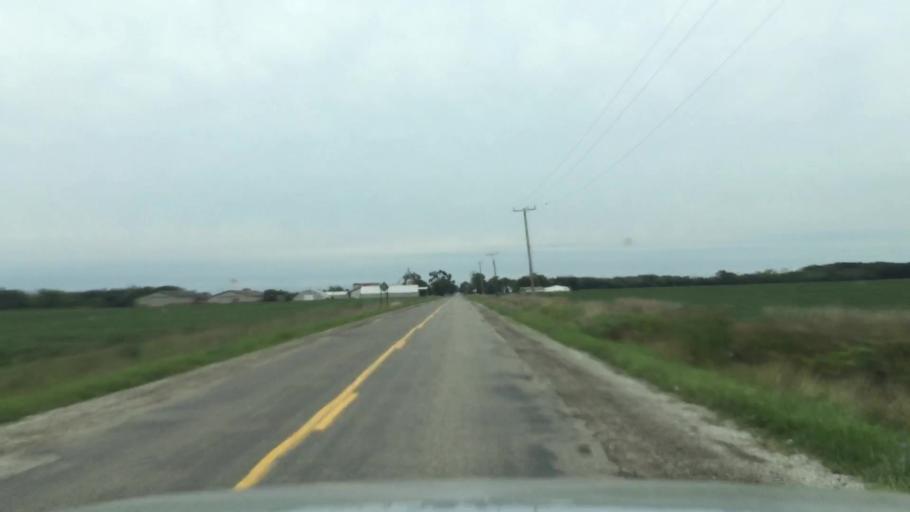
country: US
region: Michigan
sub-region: Washtenaw County
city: Milan
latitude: 42.0822
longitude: -83.7359
